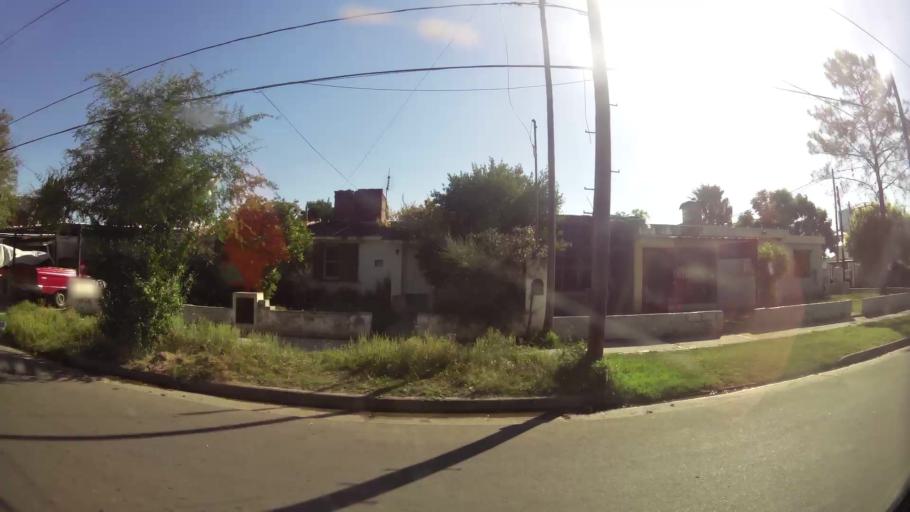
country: AR
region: Cordoba
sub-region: Departamento de Capital
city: Cordoba
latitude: -31.3610
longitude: -64.1882
